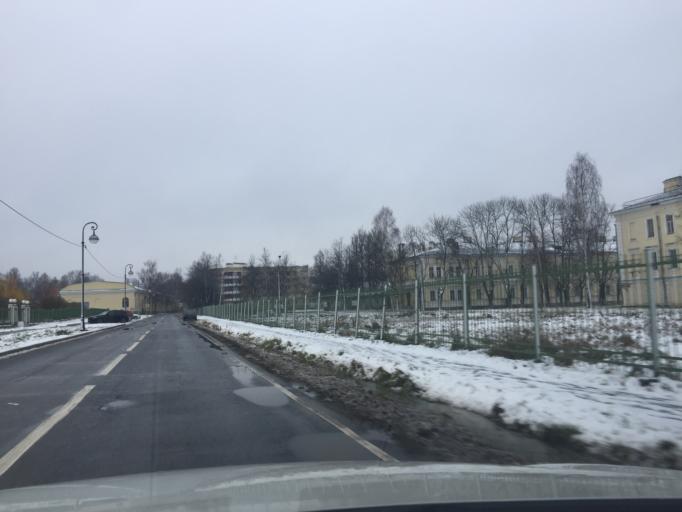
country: RU
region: St.-Petersburg
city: Pushkin
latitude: 59.7048
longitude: 30.3962
